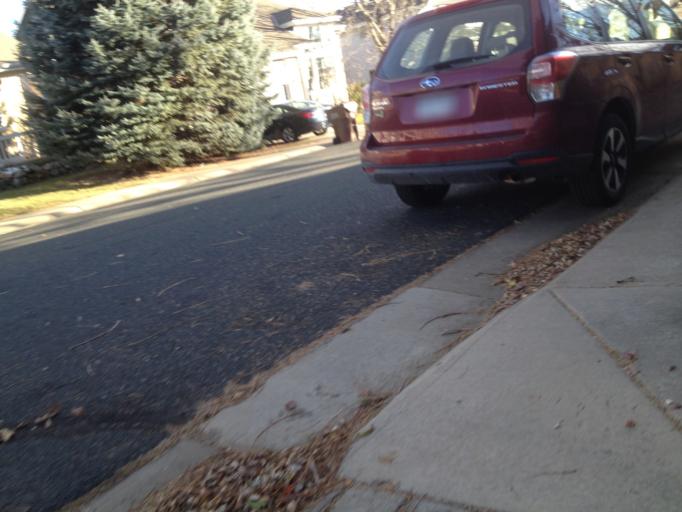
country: US
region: Colorado
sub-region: Boulder County
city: Superior
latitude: 39.9709
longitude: -105.1608
